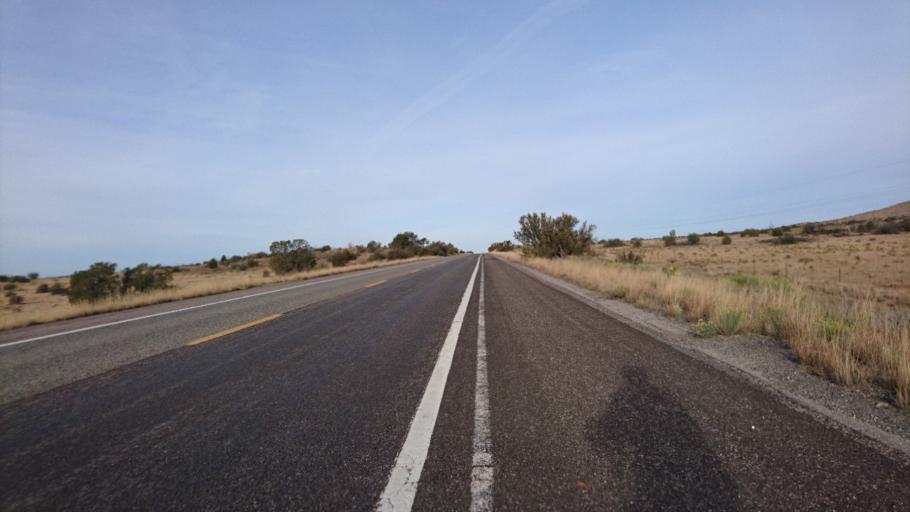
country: US
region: Arizona
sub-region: Mohave County
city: Peach Springs
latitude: 35.5339
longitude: -113.2450
